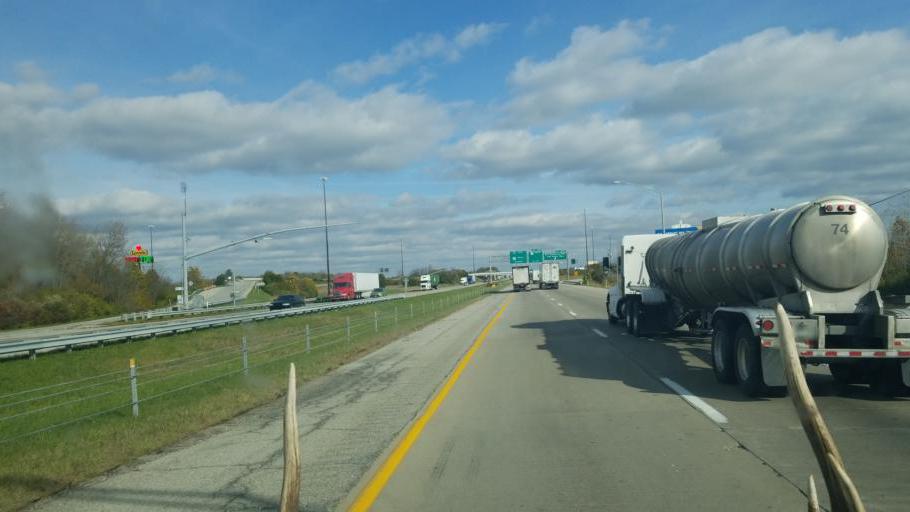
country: US
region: Indiana
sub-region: Wayne County
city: Richmond
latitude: 39.8663
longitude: -84.9333
